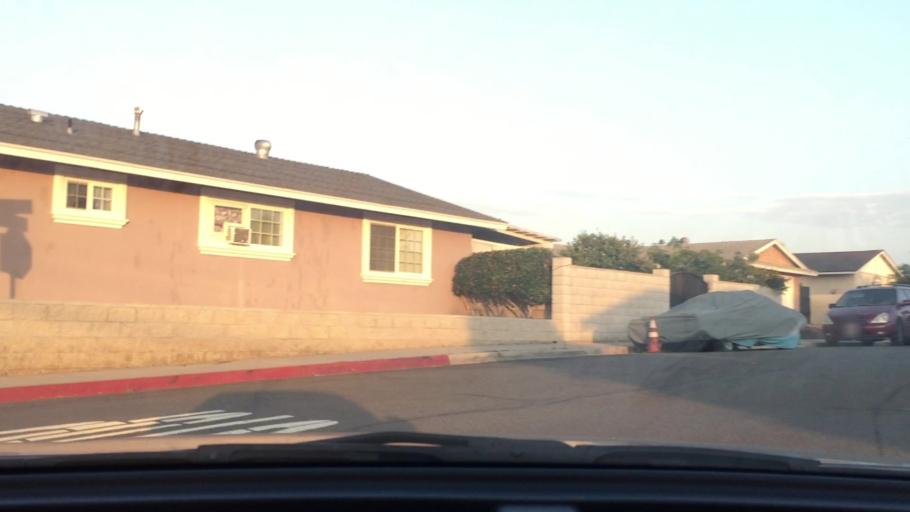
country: US
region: California
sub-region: San Diego County
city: Bonita
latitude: 32.6612
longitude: -117.0601
